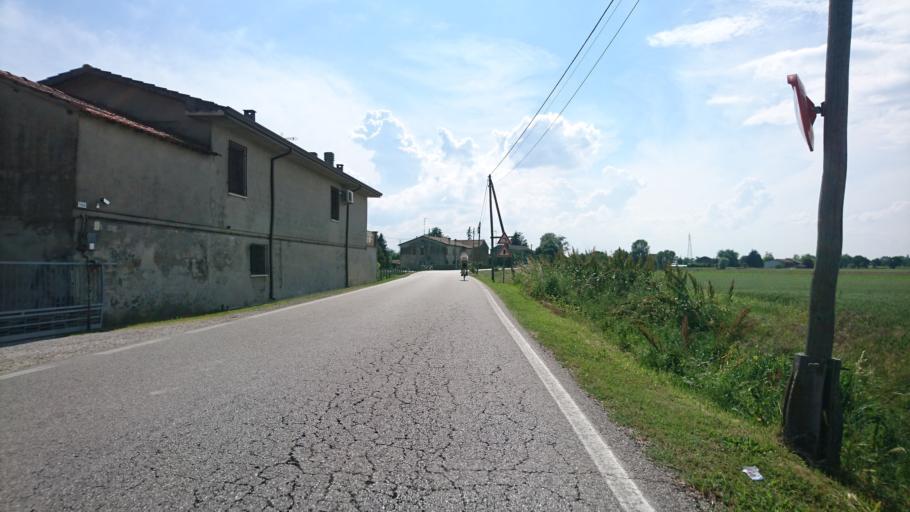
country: IT
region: Veneto
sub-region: Provincia di Rovigo
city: Castelmassa
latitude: 45.0401
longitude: 11.3156
